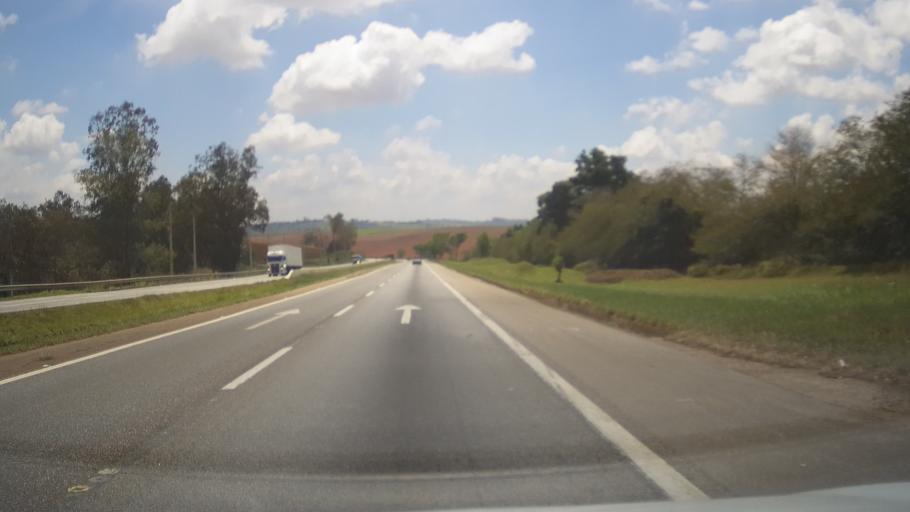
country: BR
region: Minas Gerais
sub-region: Sao Goncalo Do Sapucai
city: Sao Goncalo do Sapucai
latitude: -21.9407
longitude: -45.6168
